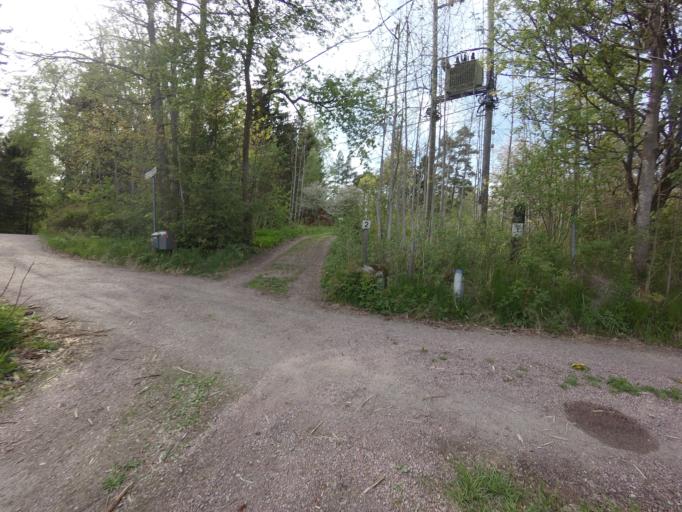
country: FI
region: Uusimaa
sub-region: Helsinki
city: Koukkuniemi
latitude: 60.1154
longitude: 24.6947
